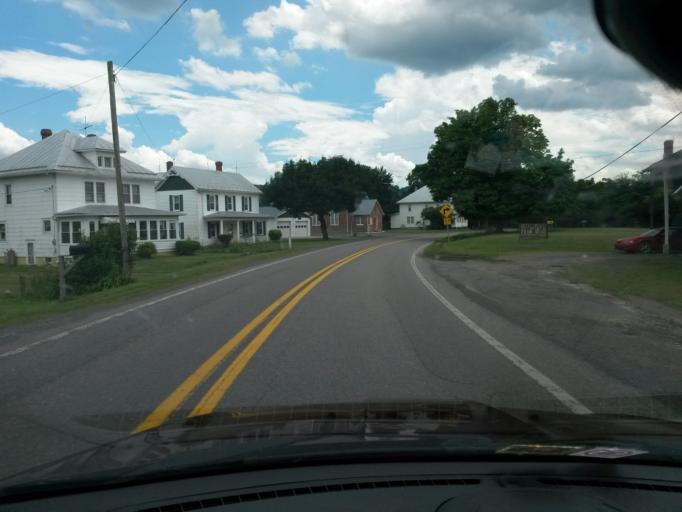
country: US
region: West Virginia
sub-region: Pendleton County
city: Franklin
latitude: 38.7884
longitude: -79.2823
